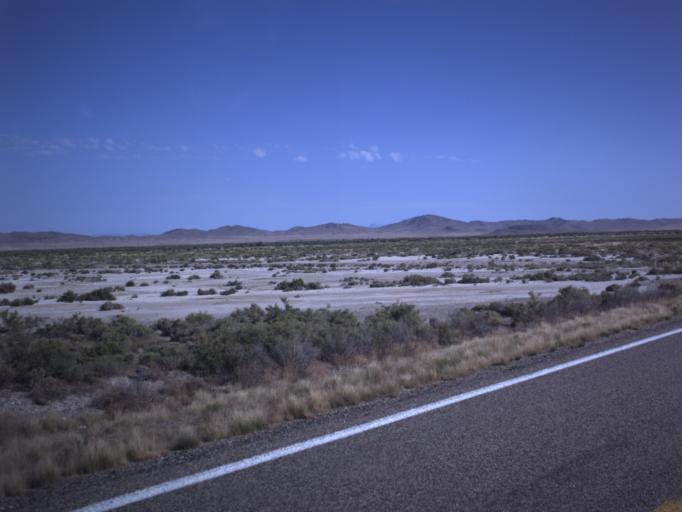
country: US
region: Utah
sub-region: Beaver County
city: Milford
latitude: 38.6126
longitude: -112.9858
